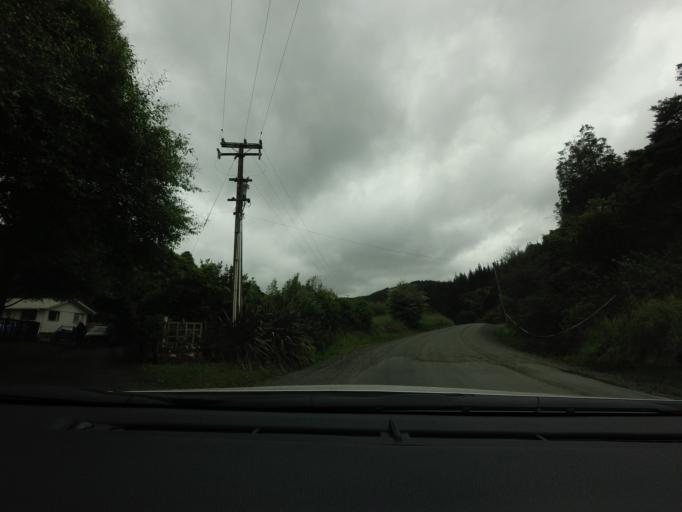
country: NZ
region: Auckland
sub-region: Auckland
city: Warkworth
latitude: -36.4935
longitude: 174.6224
